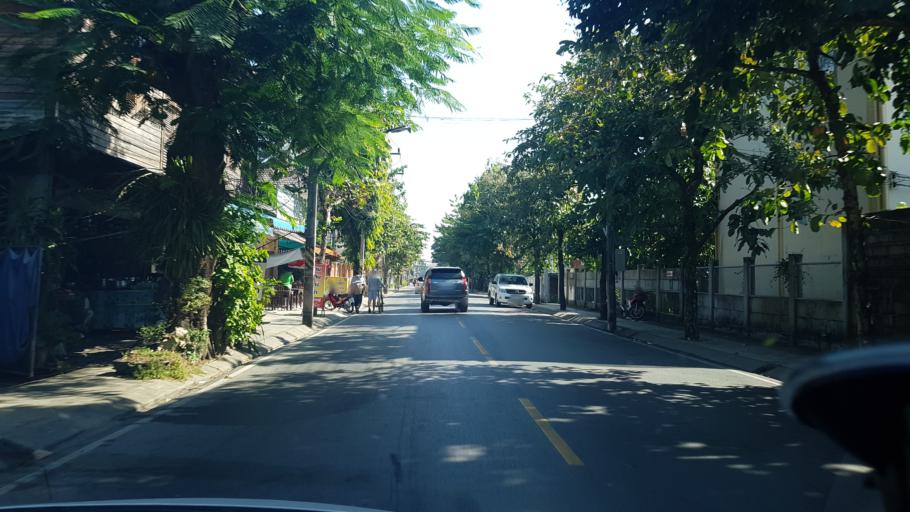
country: TH
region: Chiang Rai
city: Chiang Rai
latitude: 19.9092
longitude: 99.8249
